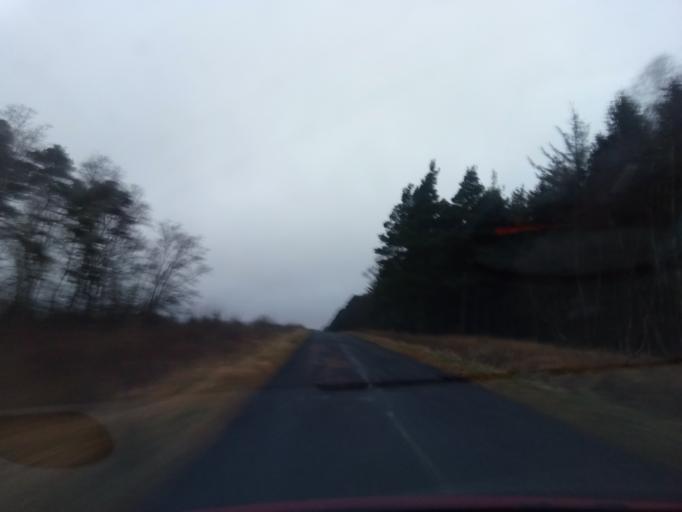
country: GB
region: England
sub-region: Northumberland
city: Rothley
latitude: 55.2039
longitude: -2.0080
